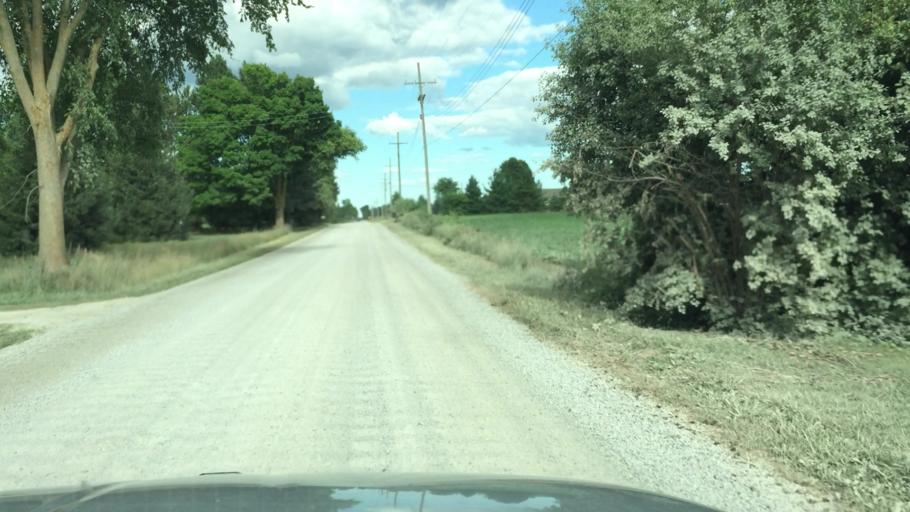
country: US
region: Michigan
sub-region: Saint Clair County
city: Yale
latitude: 43.1442
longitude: -82.8093
